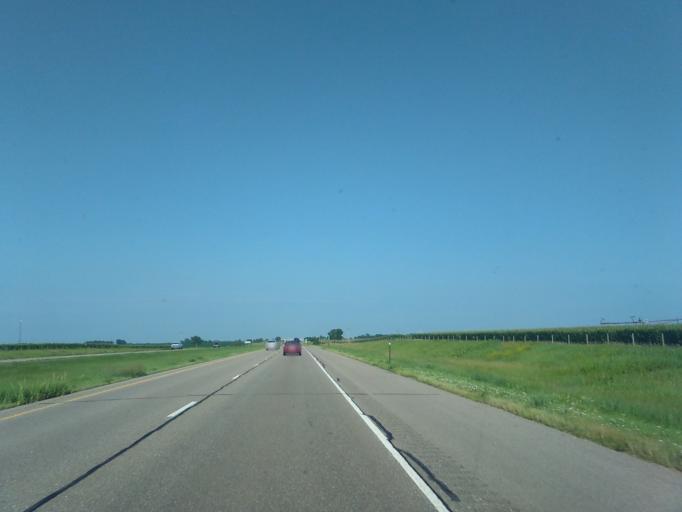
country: US
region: Nebraska
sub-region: Hamilton County
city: Aurora
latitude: 40.8221
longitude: -98.1734
